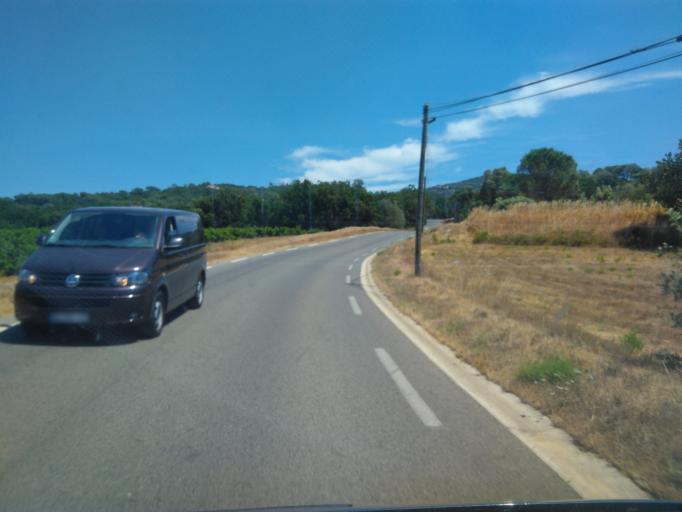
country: FR
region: Provence-Alpes-Cote d'Azur
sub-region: Departement du Var
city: Gassin
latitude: 43.2159
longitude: 6.5815
